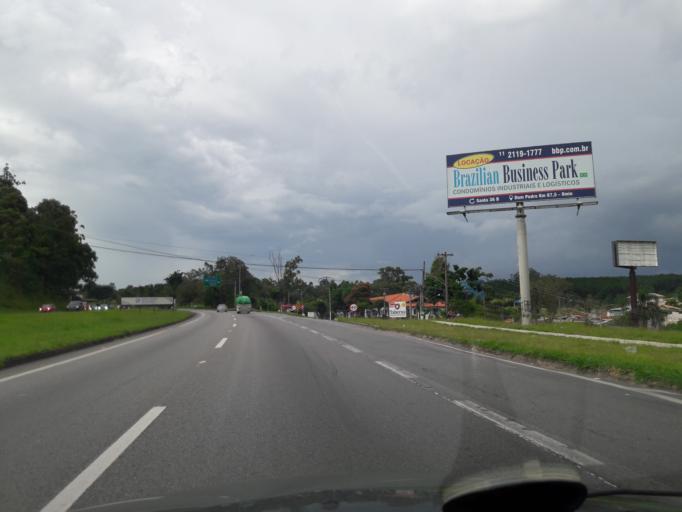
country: BR
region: Sao Paulo
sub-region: Atibaia
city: Atibaia
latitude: -23.1046
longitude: -46.5685
